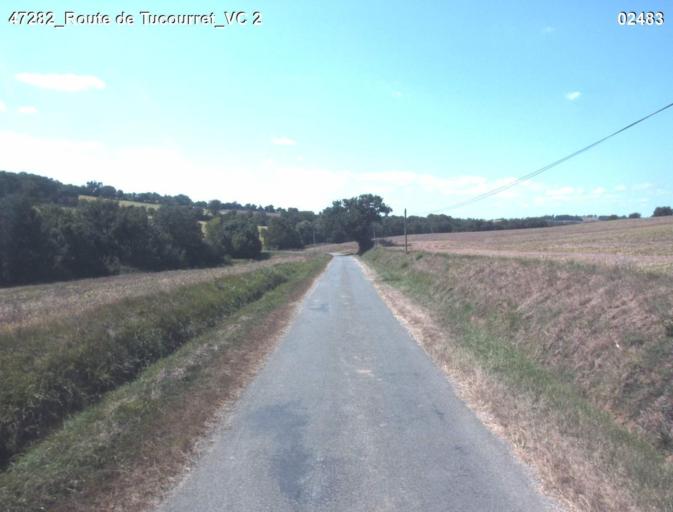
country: FR
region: Aquitaine
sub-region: Departement du Lot-et-Garonne
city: Laplume
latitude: 44.1059
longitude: 0.4963
